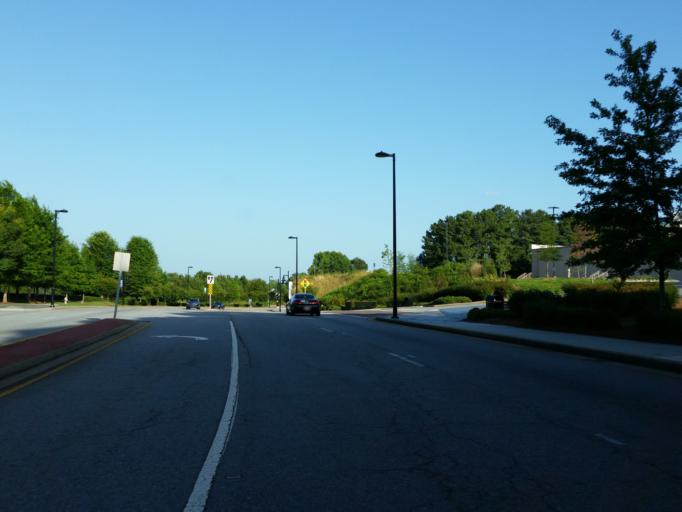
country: US
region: Georgia
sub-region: Cobb County
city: Vinings
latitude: 33.8836
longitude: -84.4590
